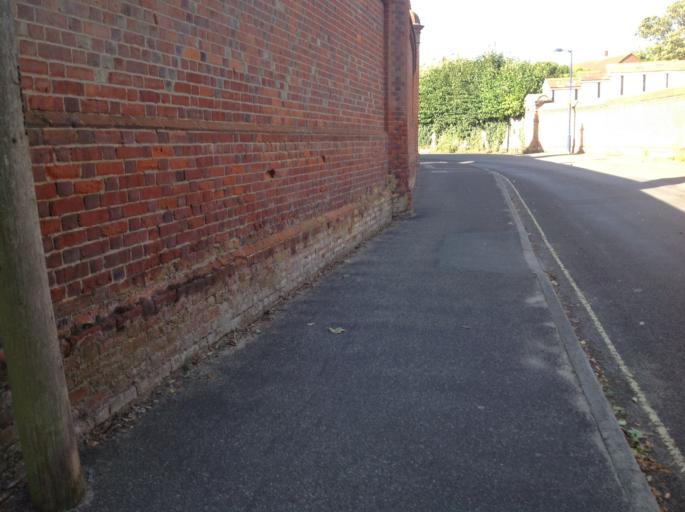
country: GB
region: England
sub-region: Suffolk
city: Felixstowe
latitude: 51.9651
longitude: 1.3686
